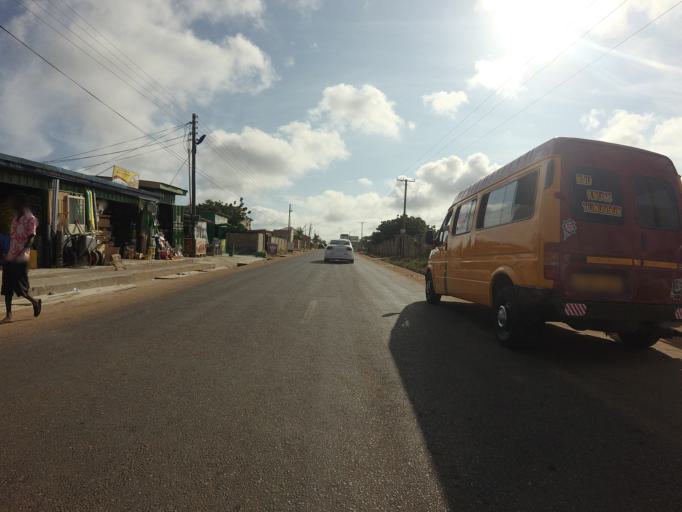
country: GH
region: Greater Accra
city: Teshi Old Town
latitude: 5.5877
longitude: -0.1385
